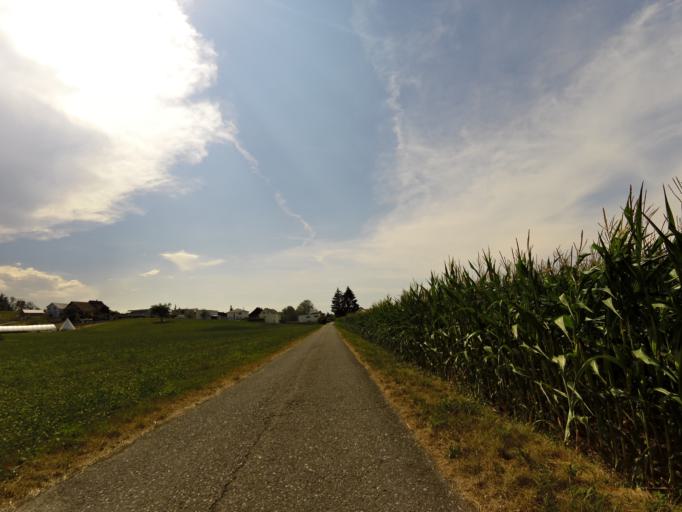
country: CH
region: Aargau
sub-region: Bezirk Lenzburg
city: Schafisheim
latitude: 47.3849
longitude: 8.1351
